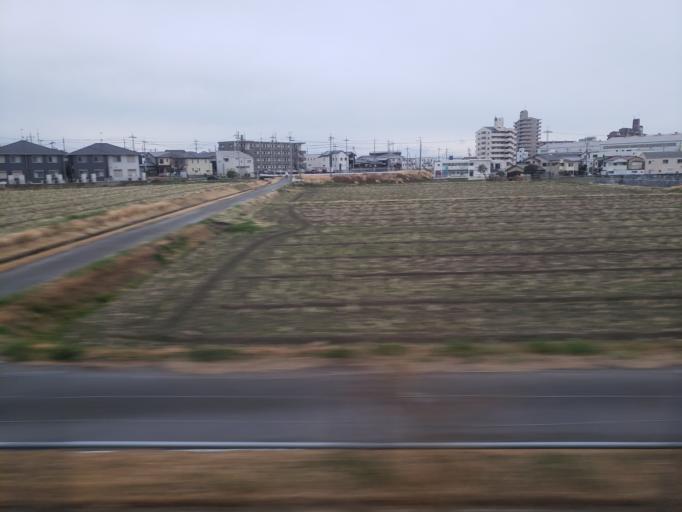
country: JP
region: Hyogo
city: Akashi
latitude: 34.6858
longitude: 134.9331
